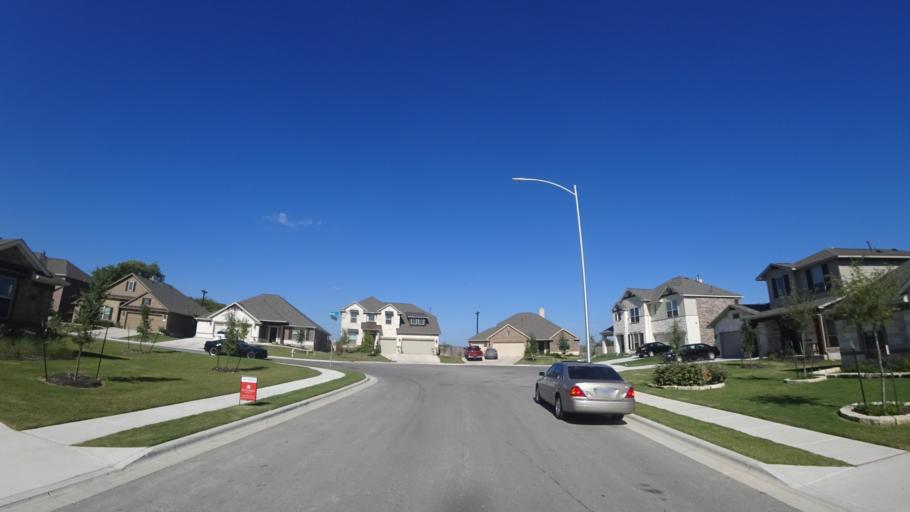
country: US
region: Texas
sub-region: Travis County
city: Manor
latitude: 30.3549
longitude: -97.5996
